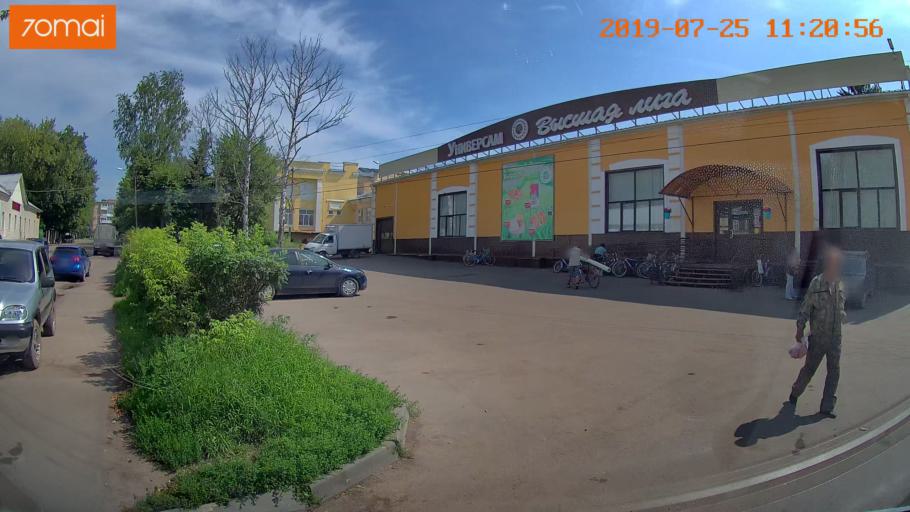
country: RU
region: Ivanovo
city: Privolzhsk
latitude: 57.3796
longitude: 41.2837
